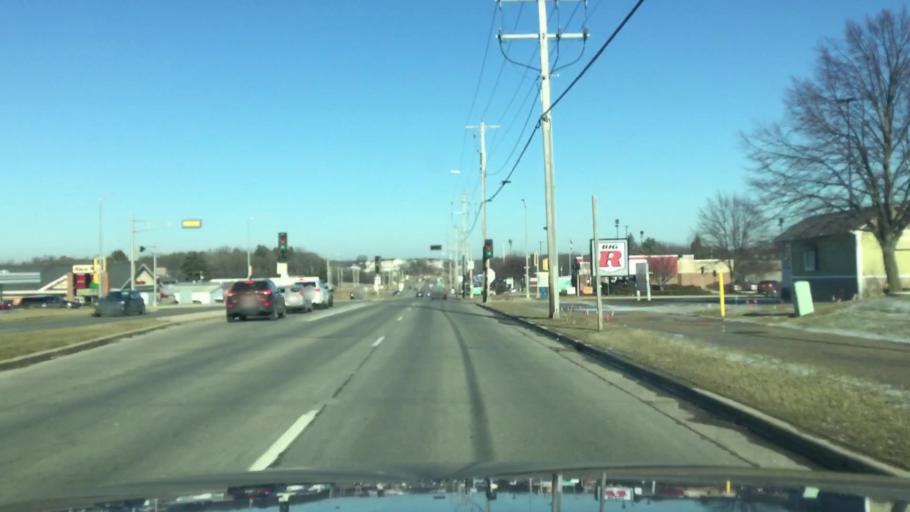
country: US
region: Wisconsin
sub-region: Racine County
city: Burlington
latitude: 42.6916
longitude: -88.2661
